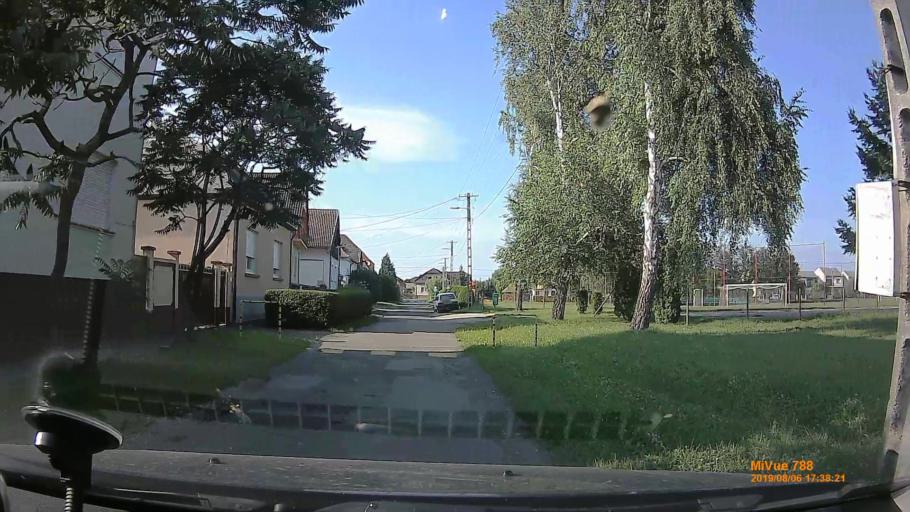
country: HU
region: Zala
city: Nagykanizsa
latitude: 46.4547
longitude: 16.9521
